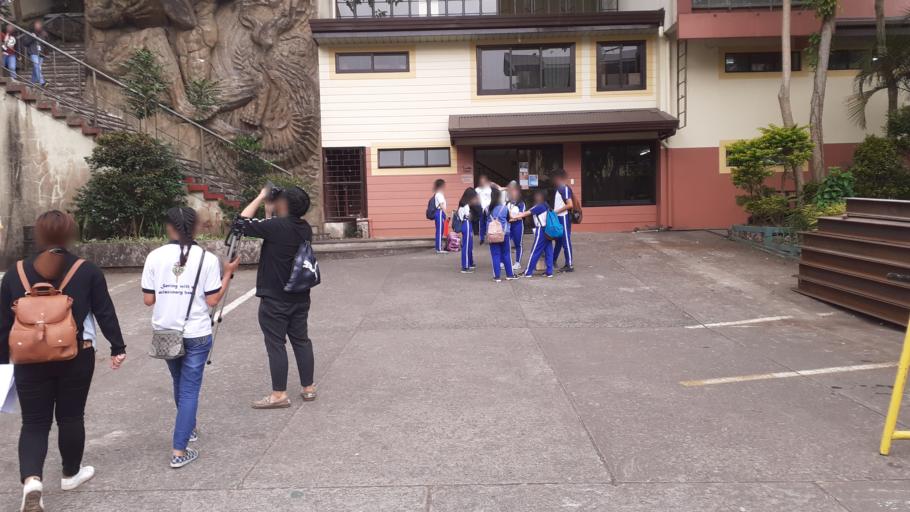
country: PH
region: Cordillera
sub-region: Baguio City
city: Baguio
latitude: 16.4183
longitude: 120.5978
